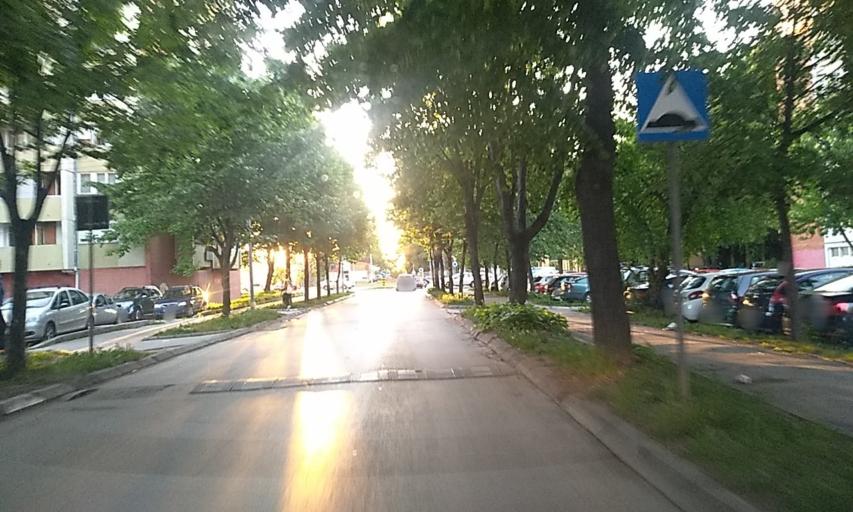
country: RS
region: Central Serbia
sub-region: Nisavski Okrug
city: Nis
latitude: 43.3241
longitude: 21.9158
